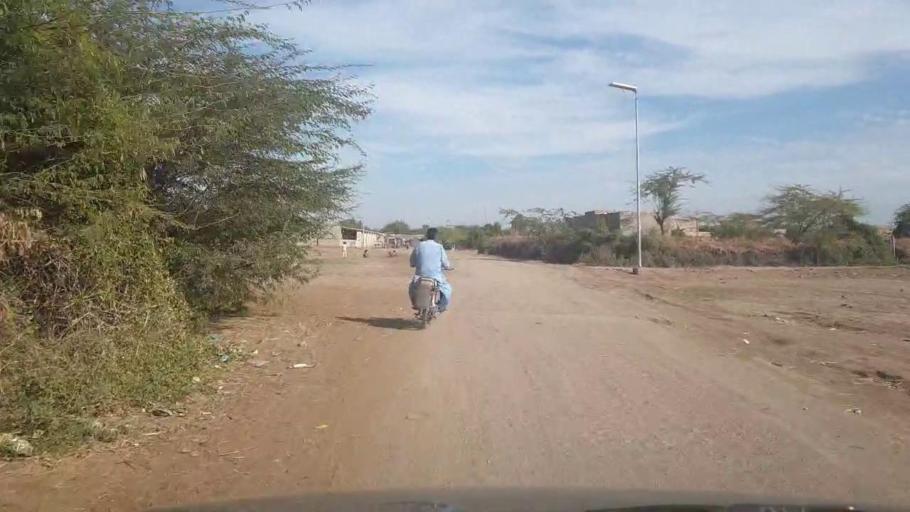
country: PK
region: Sindh
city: Pithoro
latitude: 25.3980
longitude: 69.2517
